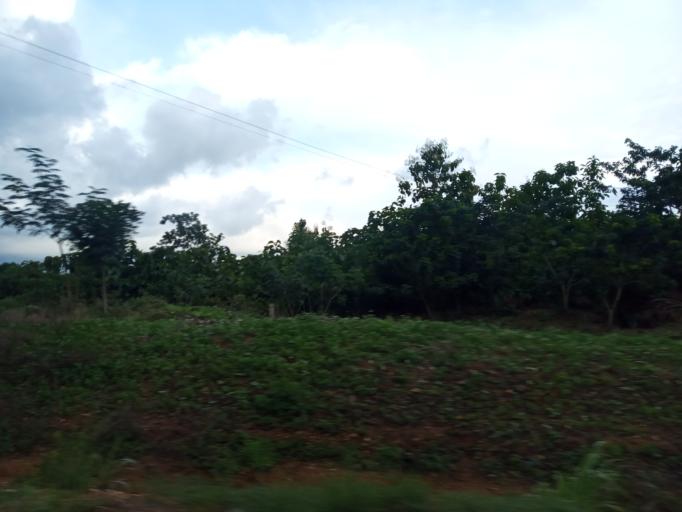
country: TG
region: Centrale
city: Sotouboua
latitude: 8.5865
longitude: 0.9888
